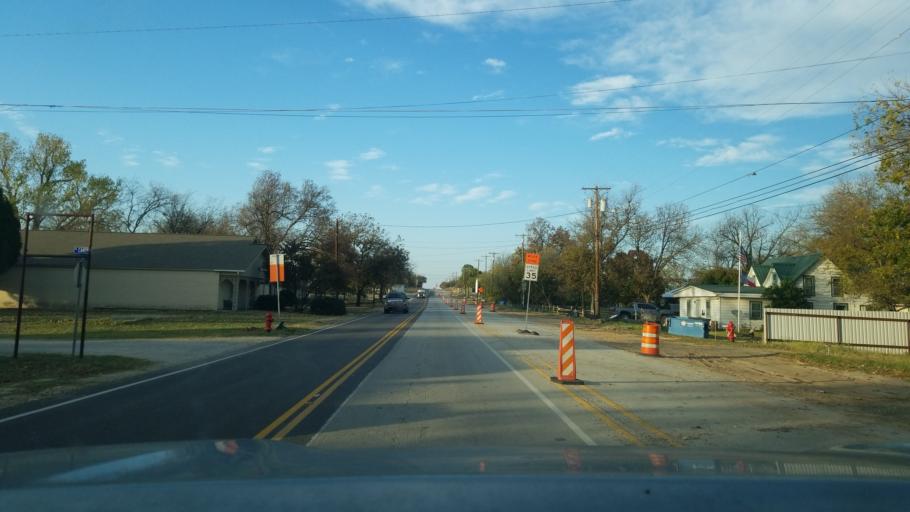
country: US
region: Texas
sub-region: Brown County
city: Lake Brownwood
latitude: 32.1029
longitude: -98.9643
